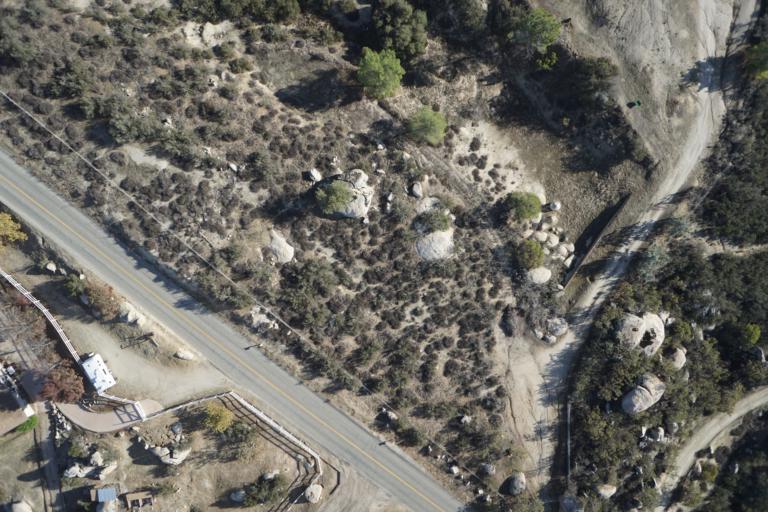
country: US
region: California
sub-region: Riverside County
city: Valle Vista
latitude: 33.6294
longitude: -116.8963
